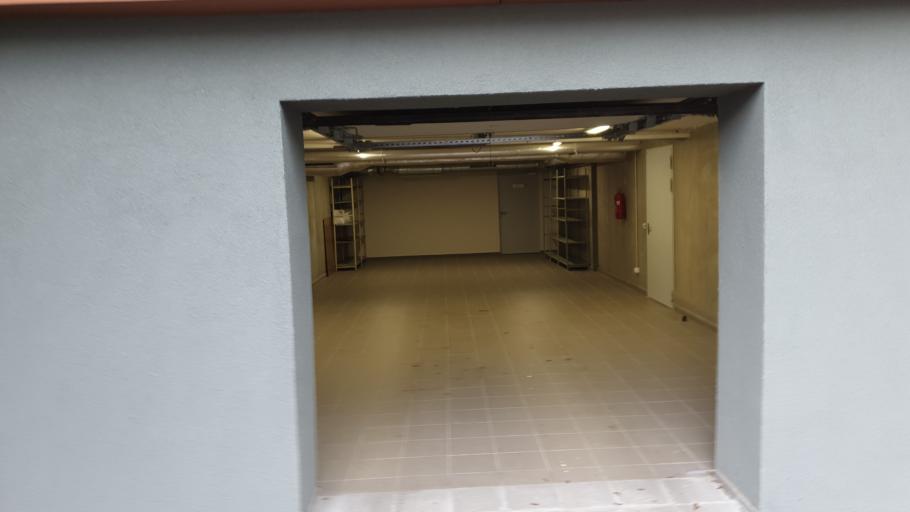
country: LT
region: Panevezys
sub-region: Panevezys City
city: Panevezys
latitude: 55.7340
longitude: 24.3553
